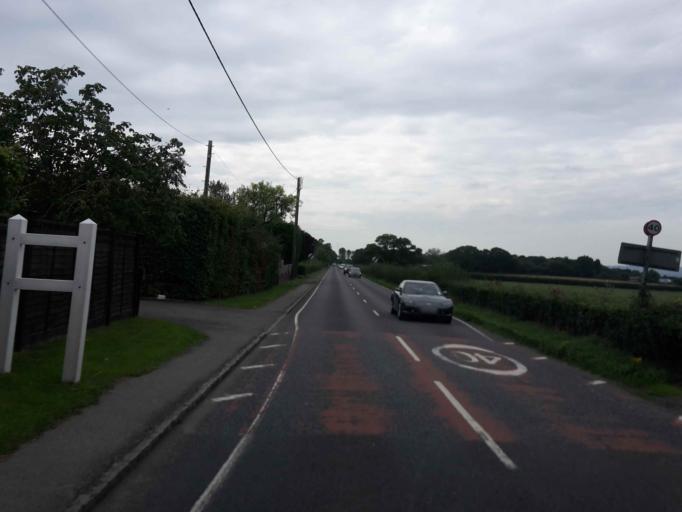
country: GB
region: England
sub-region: West Sussex
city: Billingshurst
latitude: 51.0426
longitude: -0.4368
